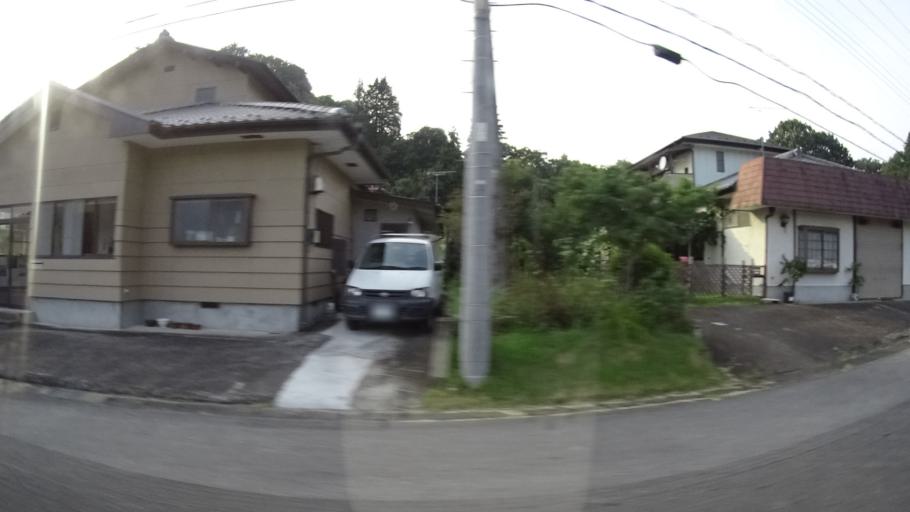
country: JP
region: Tochigi
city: Karasuyama
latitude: 36.5849
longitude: 140.1127
